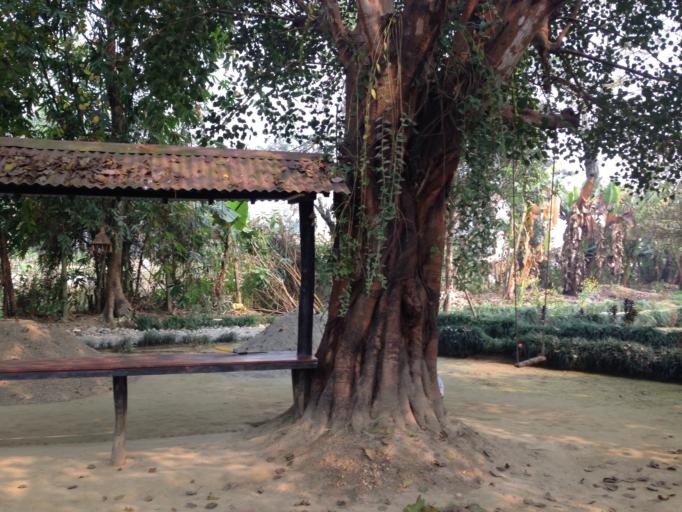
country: NP
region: Central Region
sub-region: Narayani Zone
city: Bharatpur
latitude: 27.5785
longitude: 84.4934
